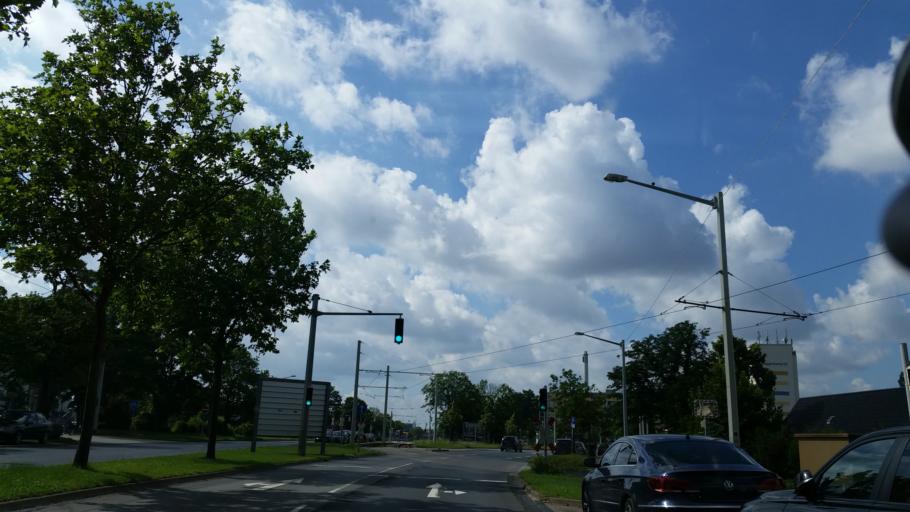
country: DE
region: Lower Saxony
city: Braunschweig
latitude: 52.2934
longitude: 10.5184
